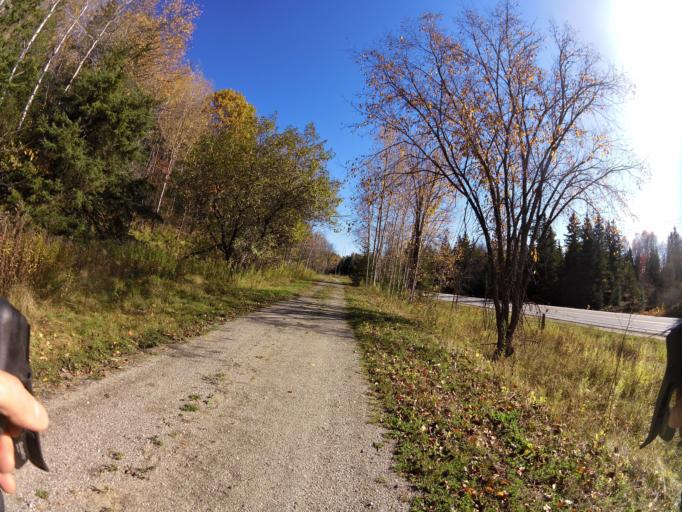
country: CA
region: Quebec
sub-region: Outaouais
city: Wakefield
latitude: 45.8459
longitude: -75.9844
